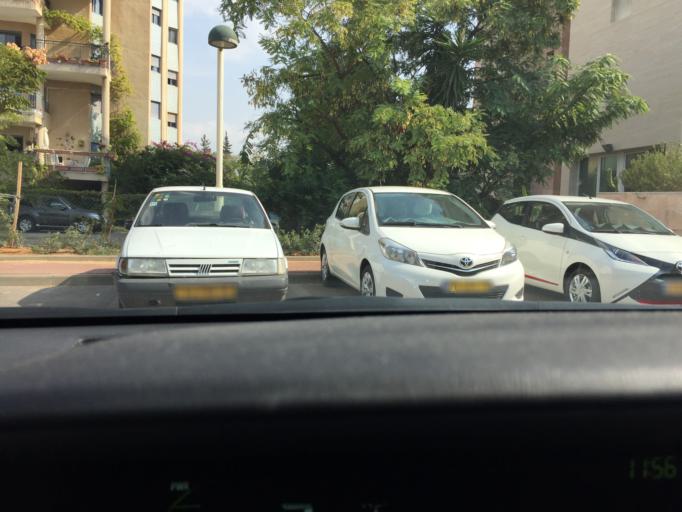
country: IL
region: Central District
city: Ganne Tiqwa
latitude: 32.0520
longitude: 34.8620
